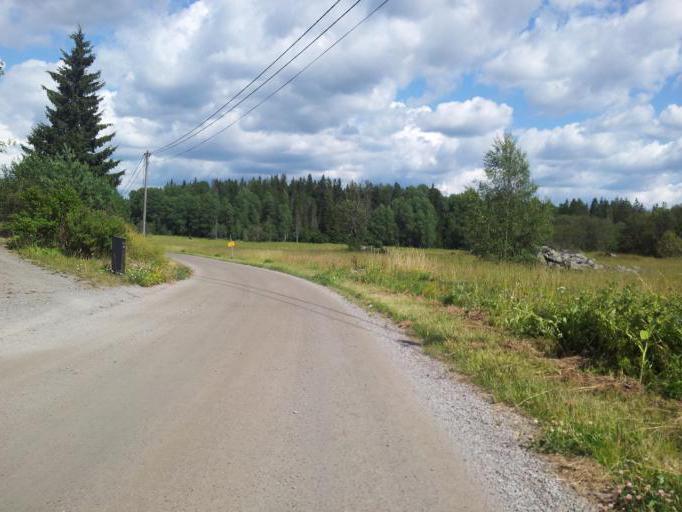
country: SE
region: Uppsala
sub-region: Knivsta Kommun
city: Knivsta
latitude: 59.8444
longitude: 17.9787
